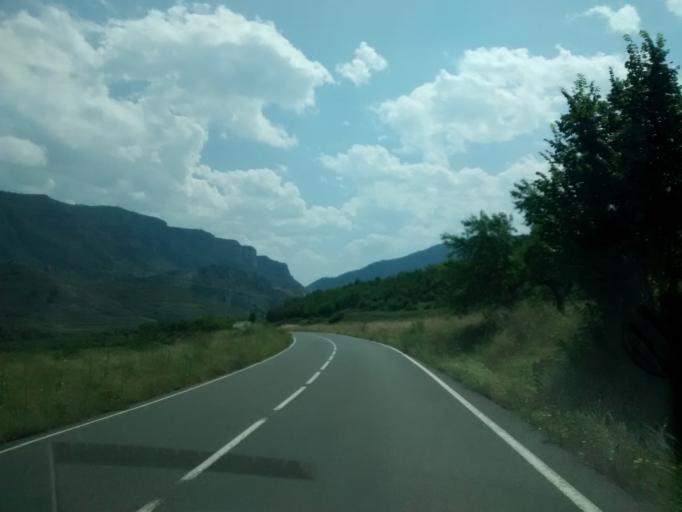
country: ES
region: La Rioja
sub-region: Provincia de La Rioja
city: Leza de Rio Leza
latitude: 42.3476
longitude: -2.3940
